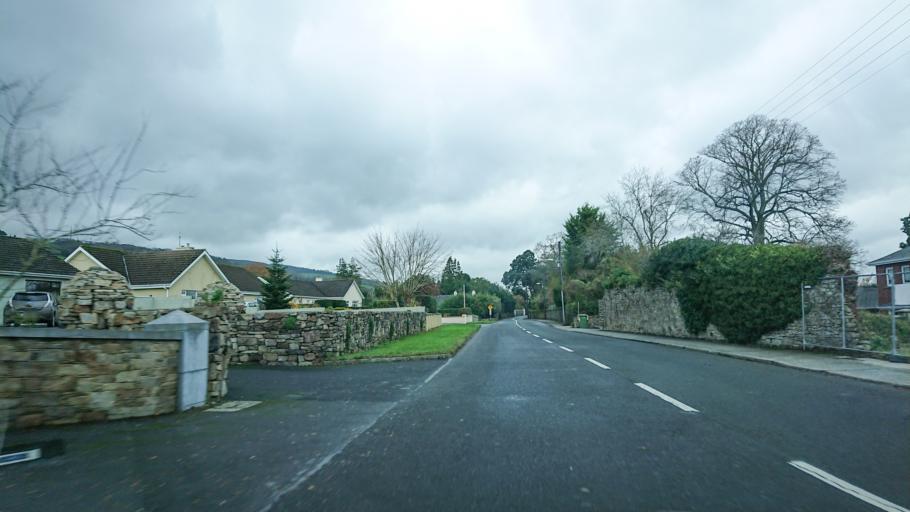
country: IE
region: Munster
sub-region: South Tipperary
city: Cluain Meala
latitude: 52.3526
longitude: -7.6801
